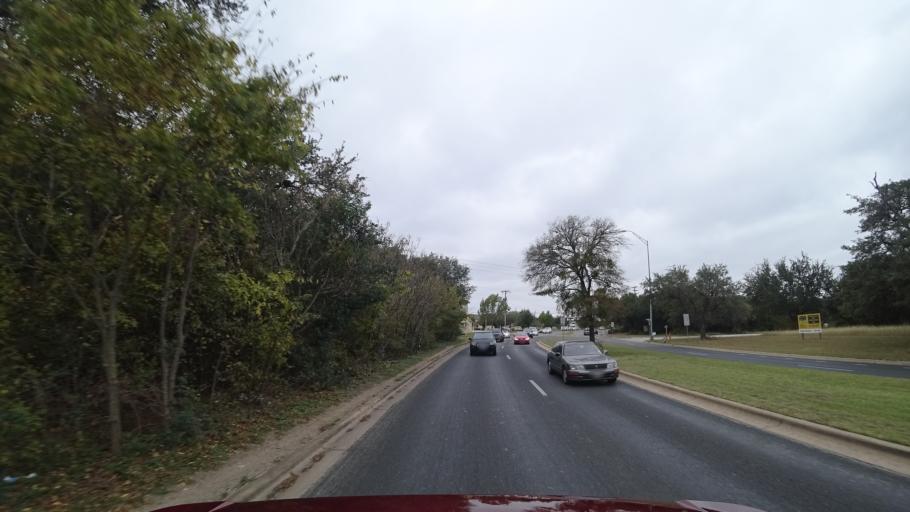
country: US
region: Texas
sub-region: Williamson County
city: Anderson Mill
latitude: 30.4751
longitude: -97.8146
